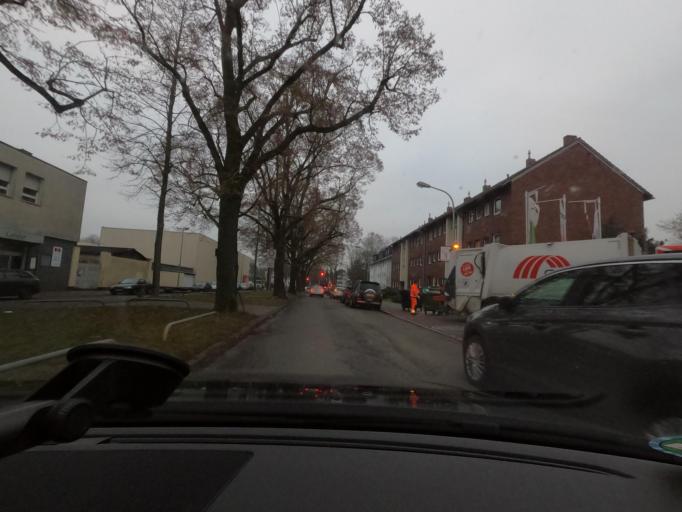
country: DE
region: North Rhine-Westphalia
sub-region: Regierungsbezirk Dusseldorf
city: Krefeld
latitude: 51.3201
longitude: 6.5499
